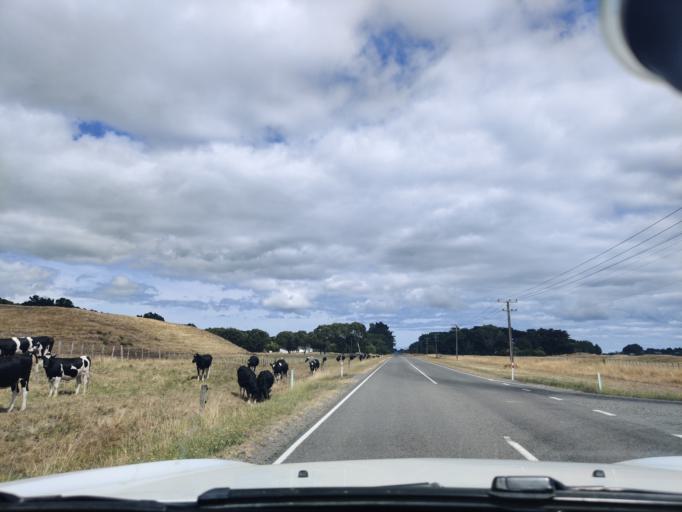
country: NZ
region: Manawatu-Wanganui
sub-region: Horowhenua District
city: Foxton
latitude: -40.4856
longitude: 175.3390
